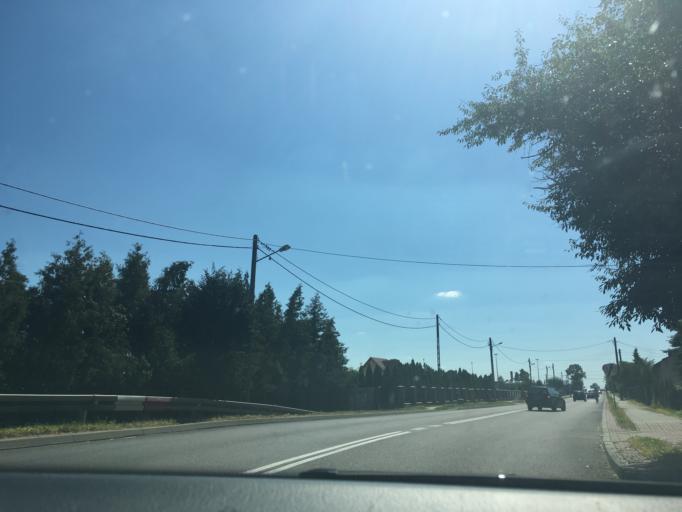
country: PL
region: Lublin Voivodeship
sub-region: Powiat janowski
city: Modliborzyce
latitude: 50.7517
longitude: 22.3337
